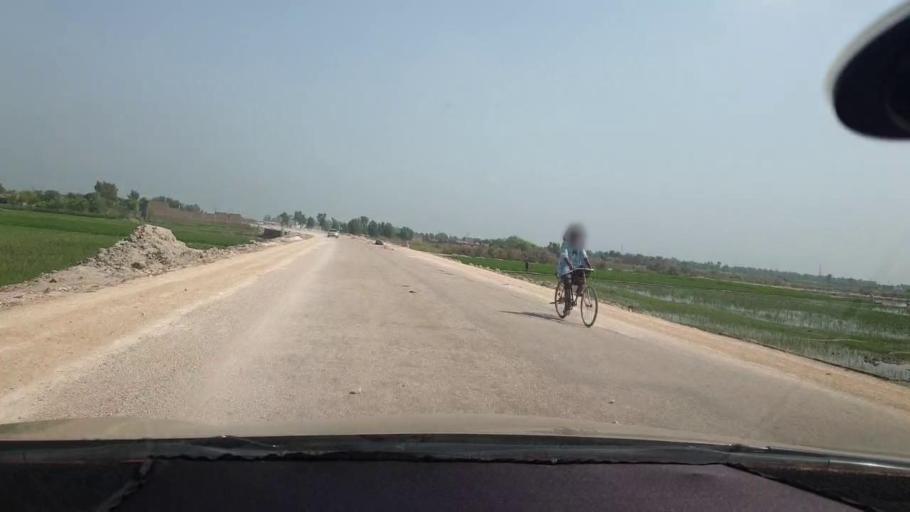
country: PK
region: Sindh
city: Kambar
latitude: 27.5834
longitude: 68.0241
